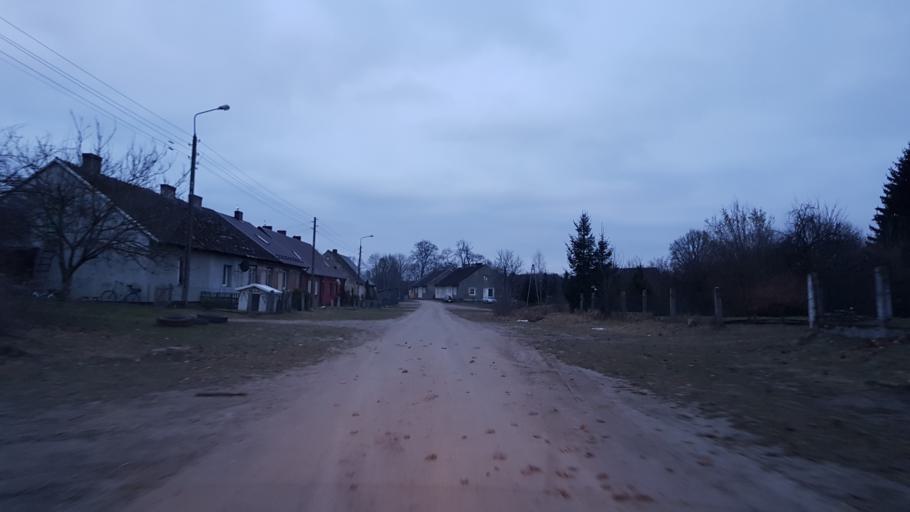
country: PL
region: Greater Poland Voivodeship
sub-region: Powiat zlotowski
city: Sypniewo
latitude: 53.4849
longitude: 16.6908
